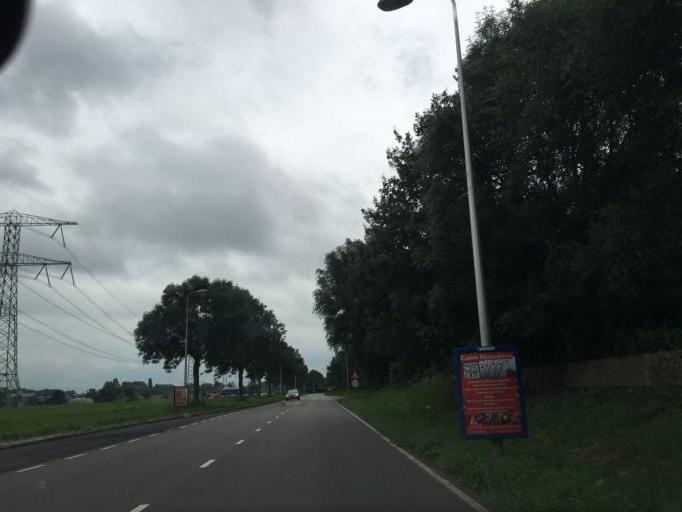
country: NL
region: South Holland
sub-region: Gemeente Capelle aan den IJssel
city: Capelle aan den IJssel
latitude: 51.9532
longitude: 4.5979
